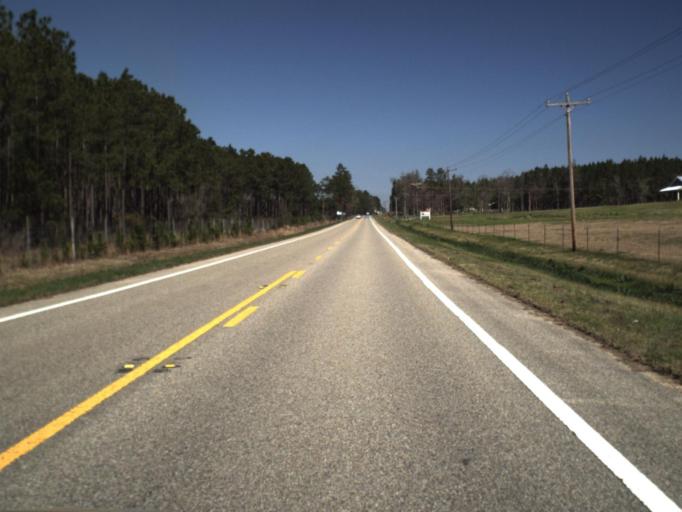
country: US
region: Florida
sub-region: Jackson County
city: Sneads
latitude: 30.6022
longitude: -85.0299
